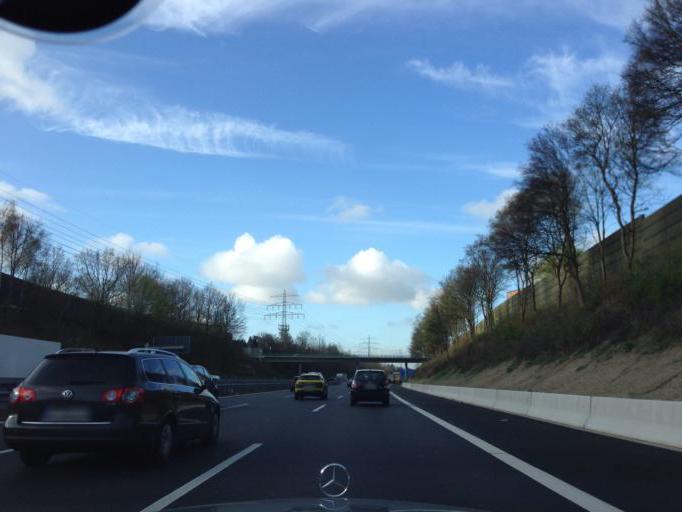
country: DE
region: Schleswig-Holstein
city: Oststeinbek
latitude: 53.5421
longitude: 10.1460
